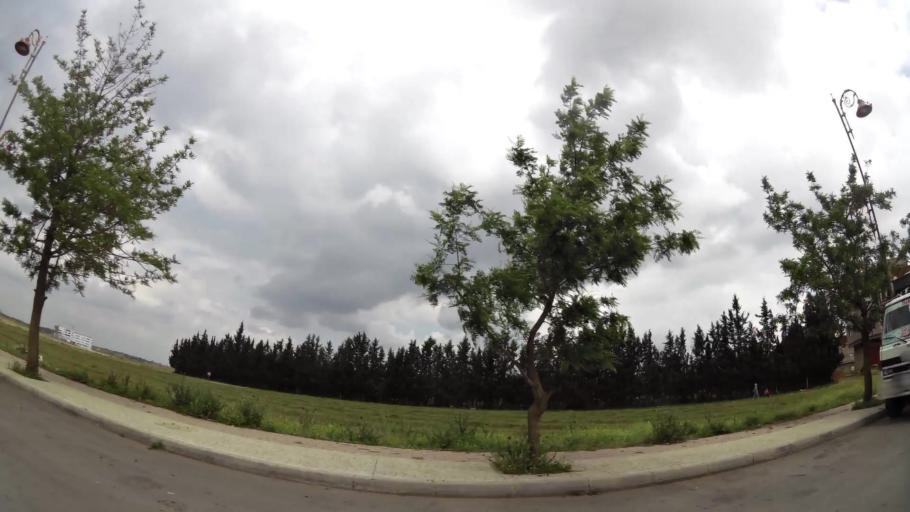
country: MA
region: Rabat-Sale-Zemmour-Zaer
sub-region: Khemisset
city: Tiflet
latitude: 33.8840
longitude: -6.3210
